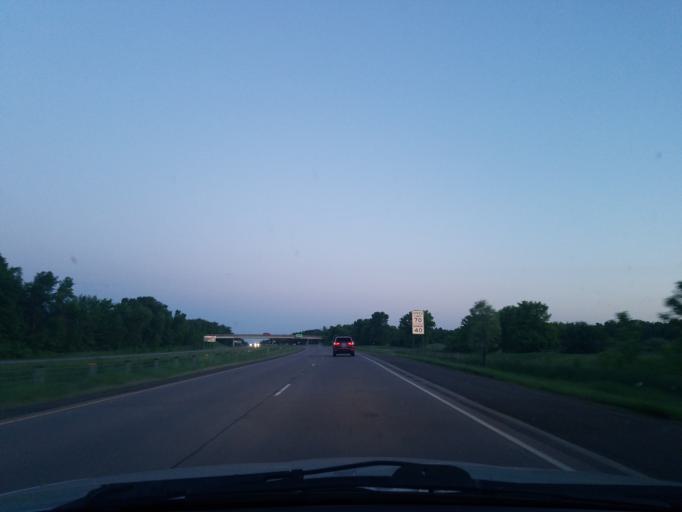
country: US
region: Minnesota
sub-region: Chisago County
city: Rush City
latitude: 45.6747
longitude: -92.9920
